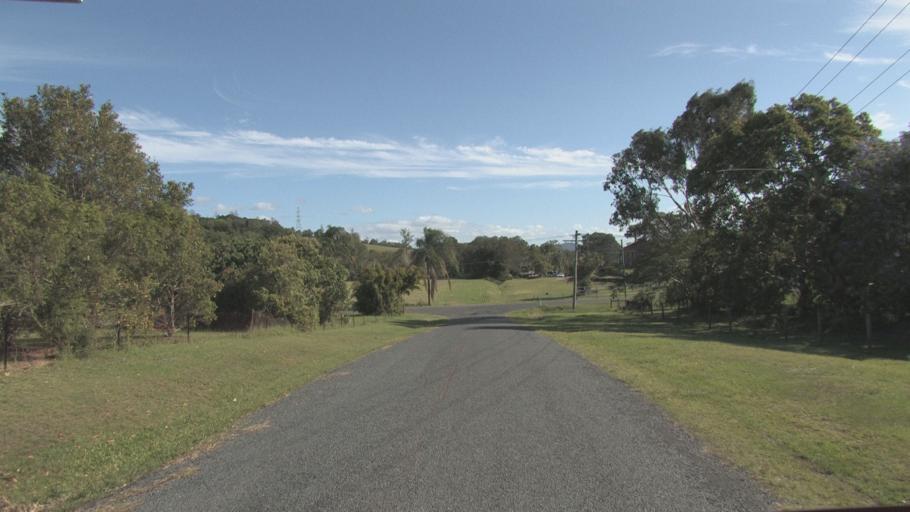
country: AU
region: Queensland
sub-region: Gold Coast
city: Yatala
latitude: -27.7130
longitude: 153.2262
